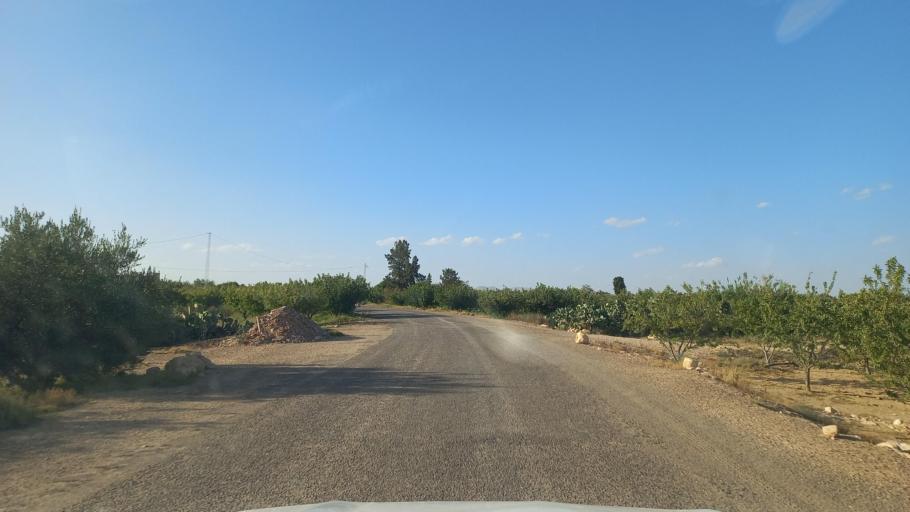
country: TN
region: Al Qasrayn
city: Kasserine
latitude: 35.2645
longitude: 9.0282
